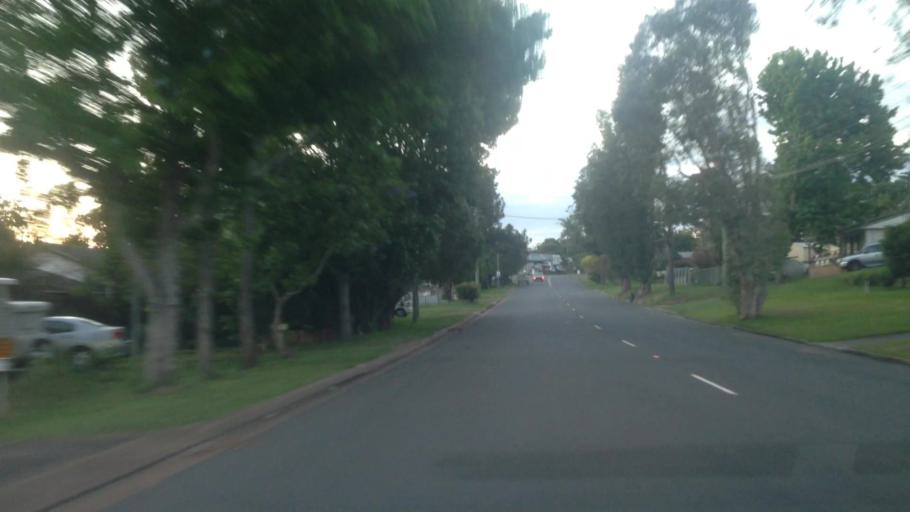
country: AU
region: New South Wales
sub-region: Lake Macquarie Shire
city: Cooranbong
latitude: -33.0709
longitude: 151.4660
